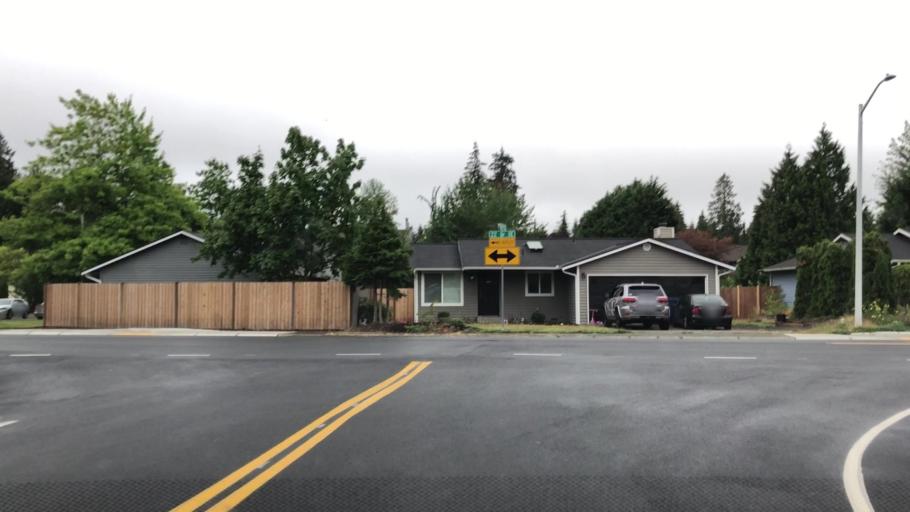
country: US
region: Washington
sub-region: Snohomish County
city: North Creek
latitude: 47.8287
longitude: -122.2025
